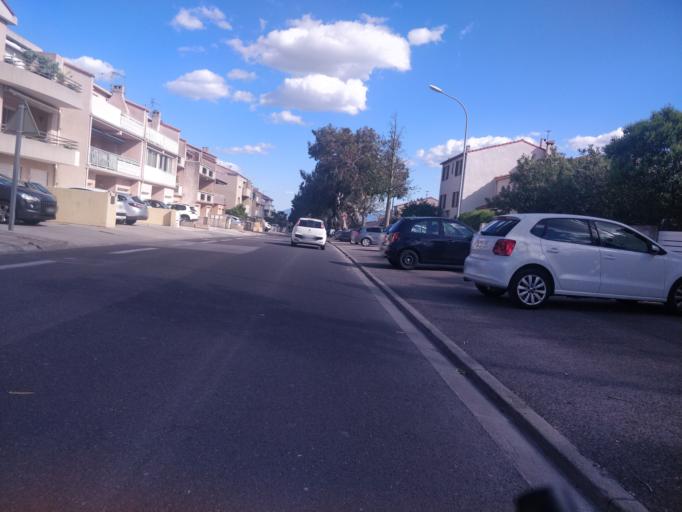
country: FR
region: Languedoc-Roussillon
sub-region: Departement des Pyrenees-Orientales
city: Perpignan
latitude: 42.6857
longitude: 2.9111
